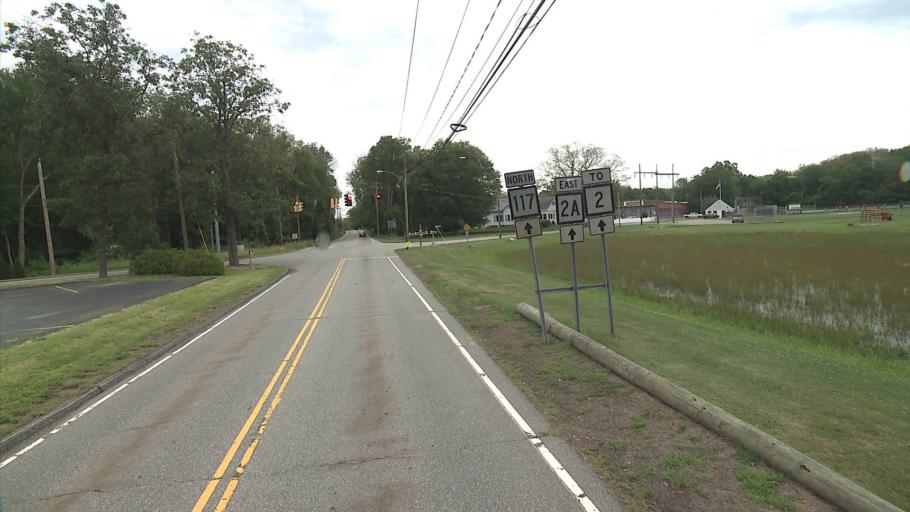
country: US
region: Connecticut
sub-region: New London County
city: Ledyard Center
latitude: 41.4872
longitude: -72.0350
